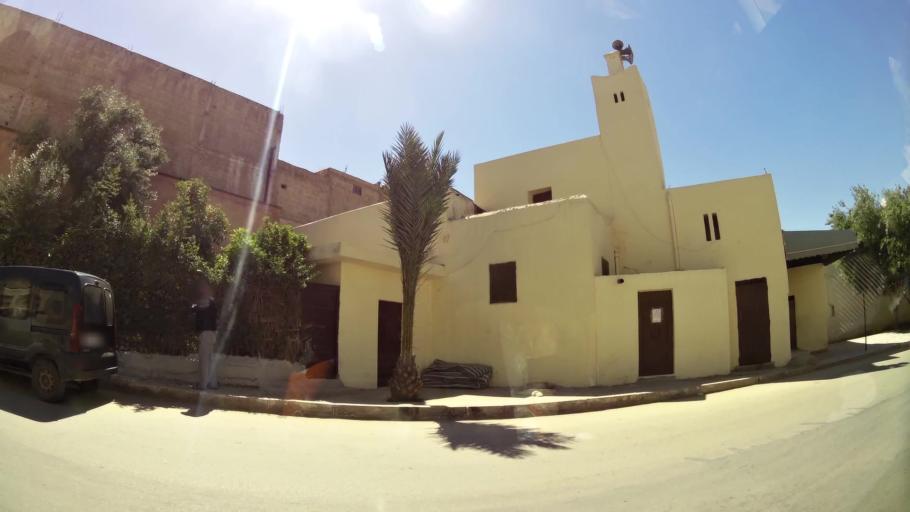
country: MA
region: Meknes-Tafilalet
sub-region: Meknes
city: Meknes
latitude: 33.8625
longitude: -5.5518
